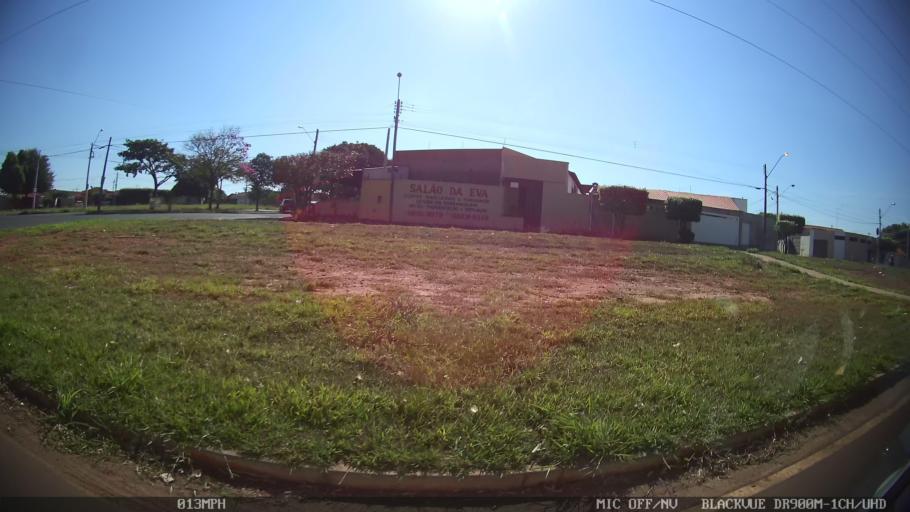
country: BR
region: Sao Paulo
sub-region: Sao Jose Do Rio Preto
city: Sao Jose do Rio Preto
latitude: -20.7640
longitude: -49.3626
